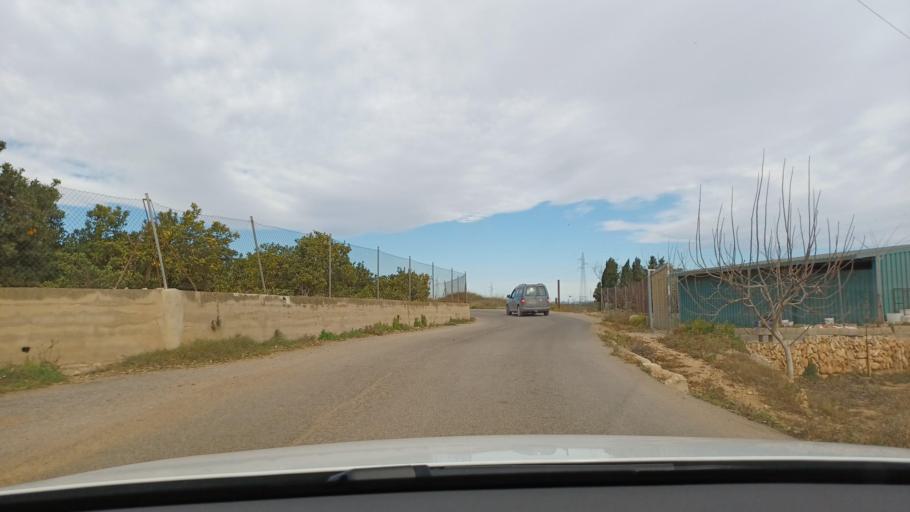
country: ES
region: Valencia
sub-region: Provincia de Valencia
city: Benifaio
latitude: 39.2899
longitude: -0.4348
